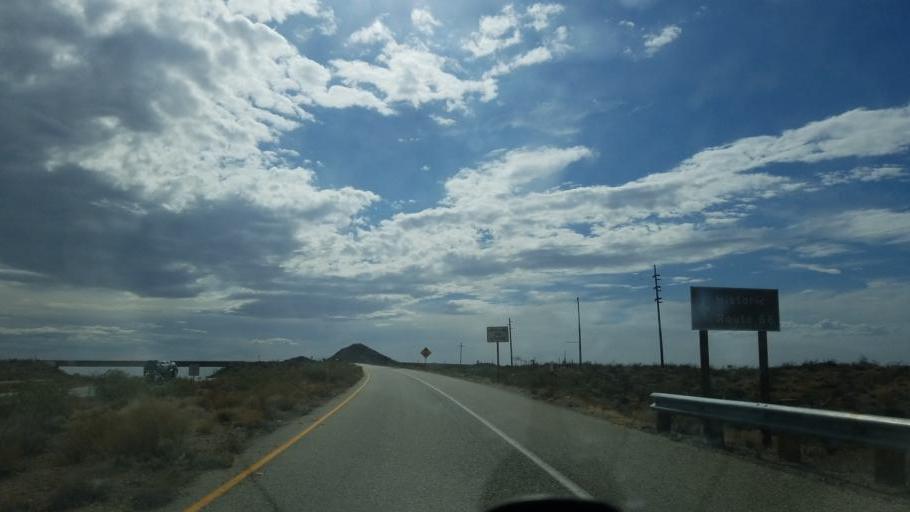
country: US
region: California
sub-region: San Bernardino County
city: Needles
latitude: 34.8310
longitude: -115.0474
